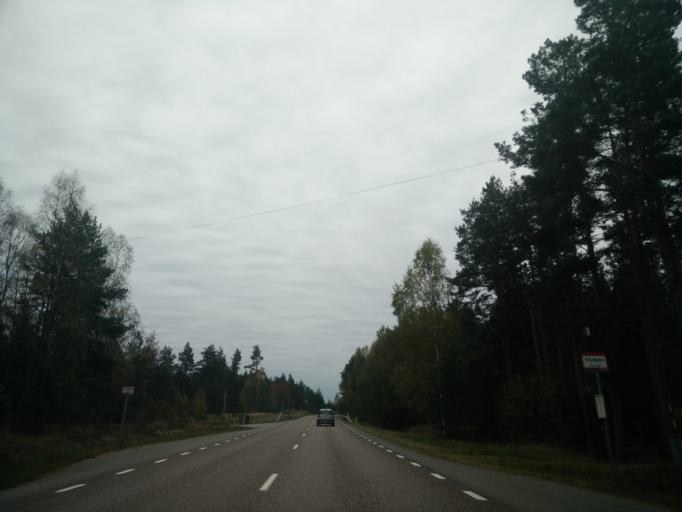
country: SE
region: Gaevleborg
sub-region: Gavle Kommun
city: Norrsundet
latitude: 60.8289
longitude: 17.2102
